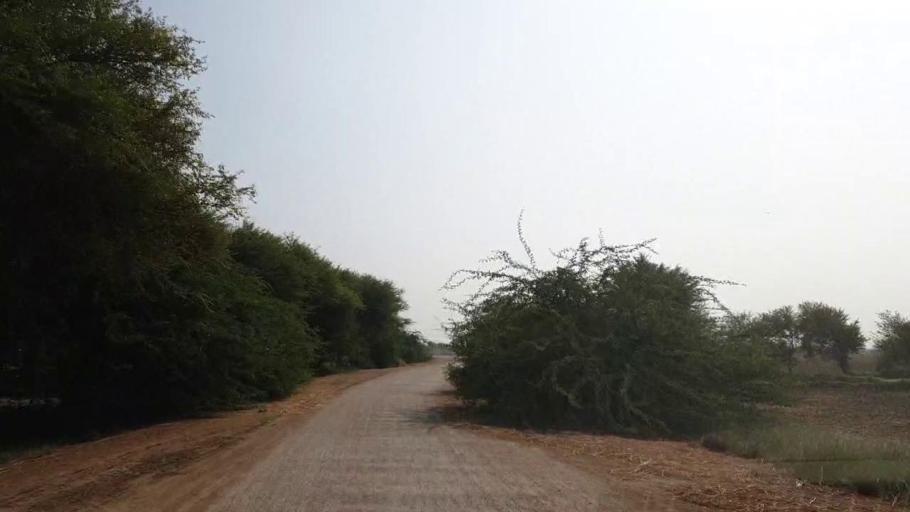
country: PK
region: Sindh
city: Matli
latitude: 24.9914
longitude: 68.5780
